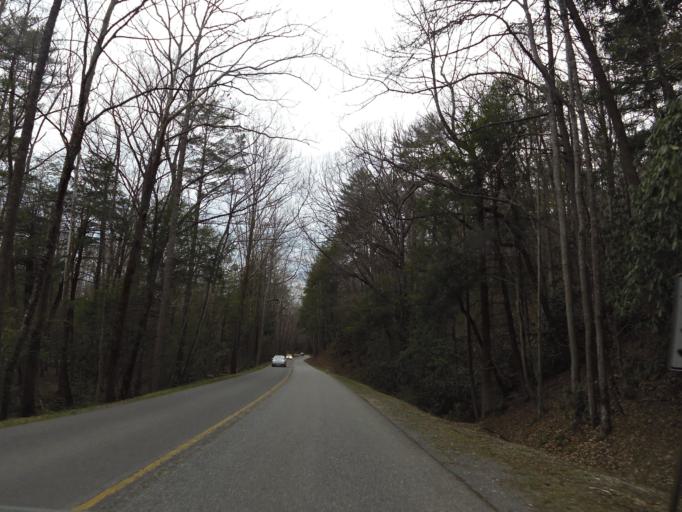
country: US
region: Tennessee
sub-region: Blount County
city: Wildwood
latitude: 35.6059
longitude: -83.7699
